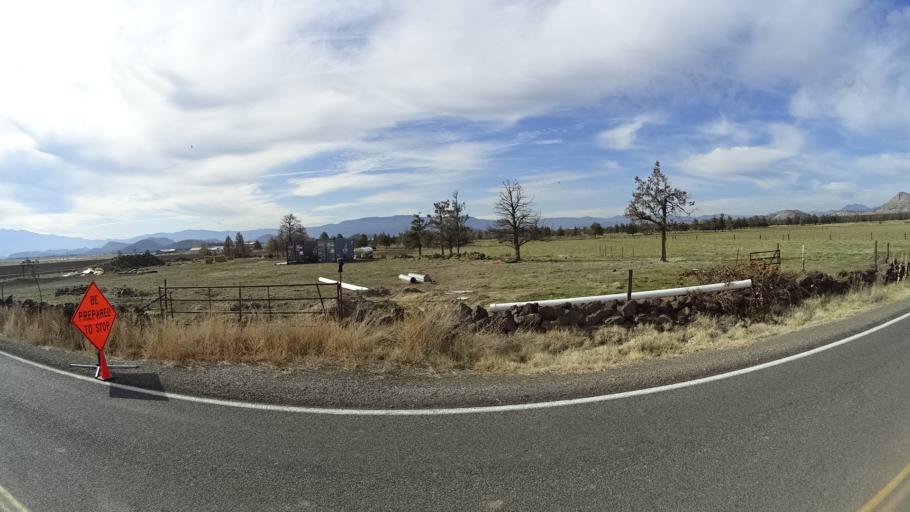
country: US
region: California
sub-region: Siskiyou County
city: Montague
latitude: 41.6267
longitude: -122.3996
